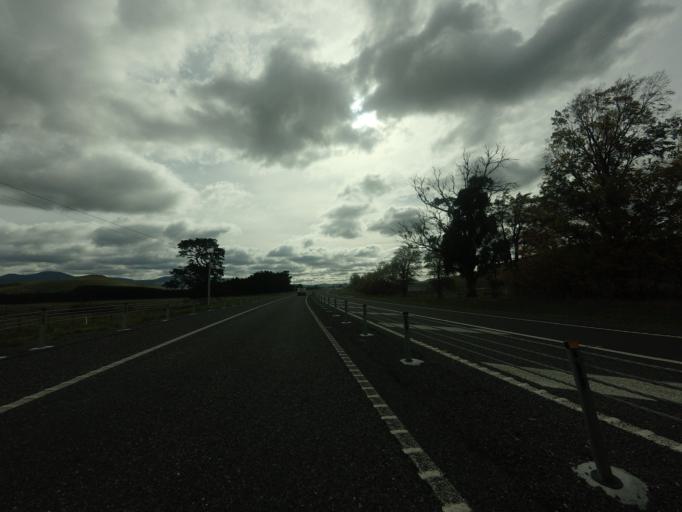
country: AU
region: Tasmania
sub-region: Brighton
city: Bridgewater
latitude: -42.5179
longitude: 147.1908
